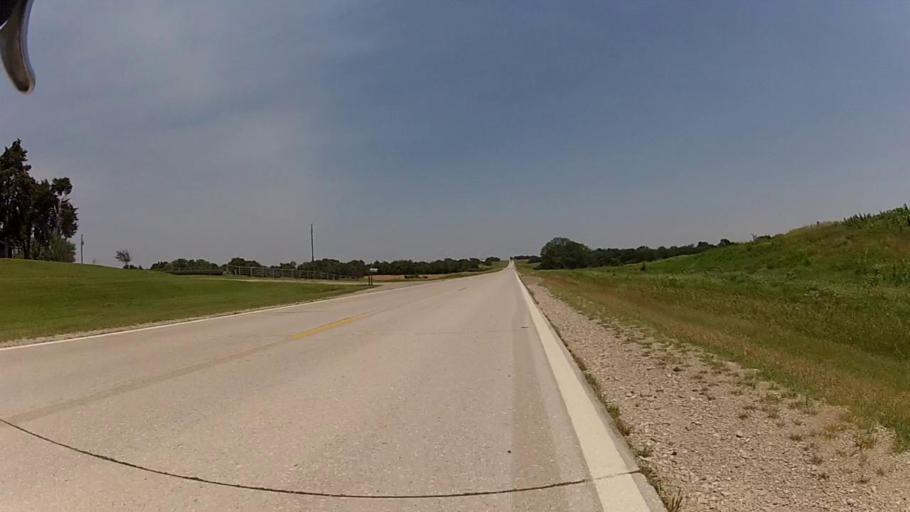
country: US
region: Kansas
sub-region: Sumner County
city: Wellington
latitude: 37.0571
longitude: -97.3732
